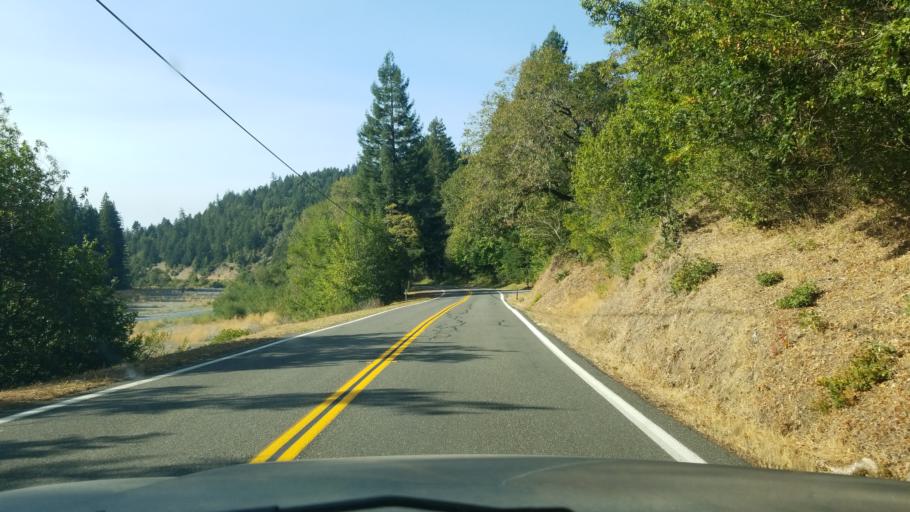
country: US
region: California
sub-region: Humboldt County
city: Redway
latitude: 40.1974
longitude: -123.7742
